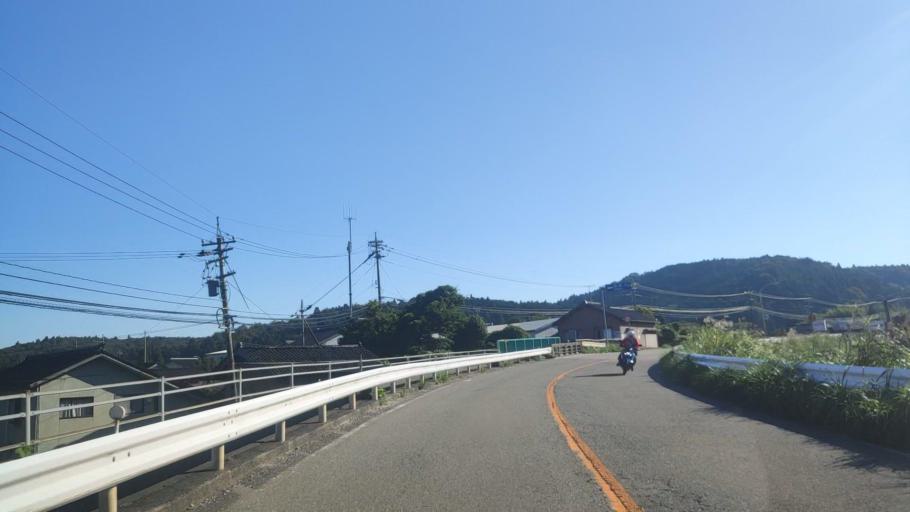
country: JP
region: Ishikawa
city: Nanao
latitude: 37.1439
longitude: 136.8721
